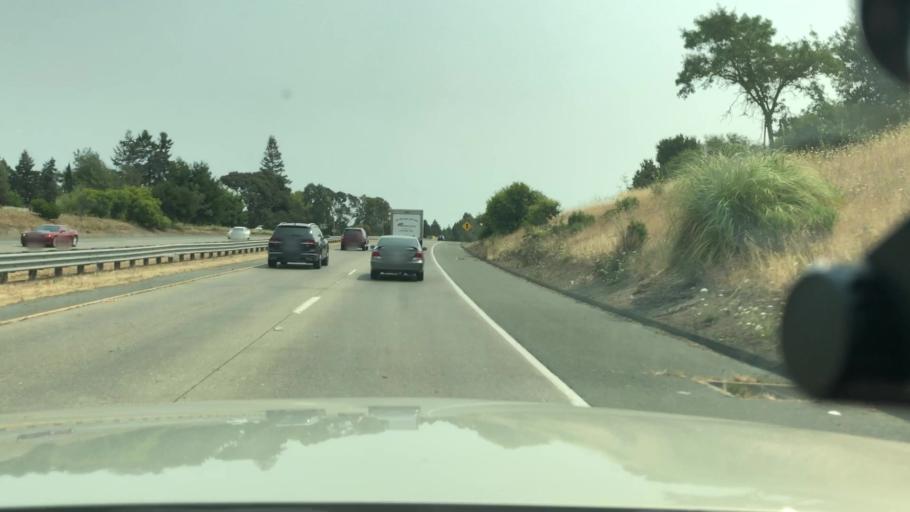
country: US
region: California
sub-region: Sonoma County
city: Roseland
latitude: 38.4307
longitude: -122.7409
